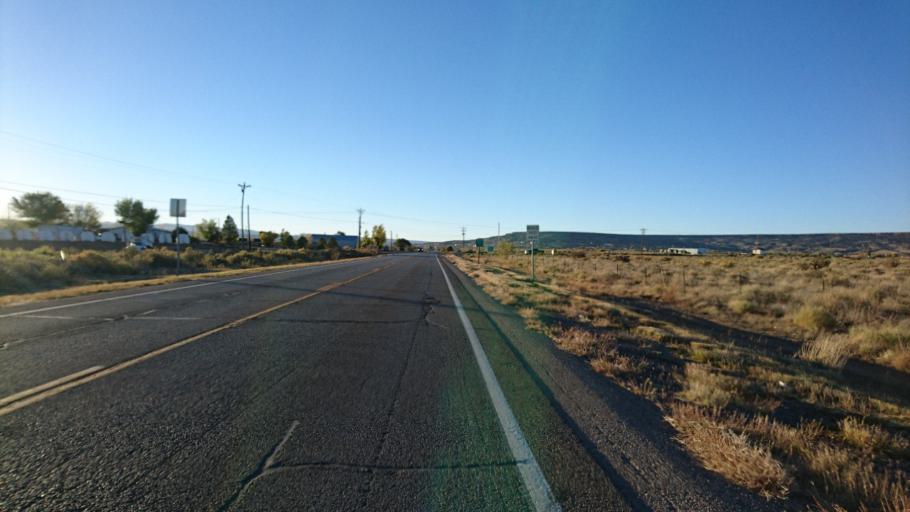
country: US
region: New Mexico
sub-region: Cibola County
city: Grants
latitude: 35.1340
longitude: -107.8170
